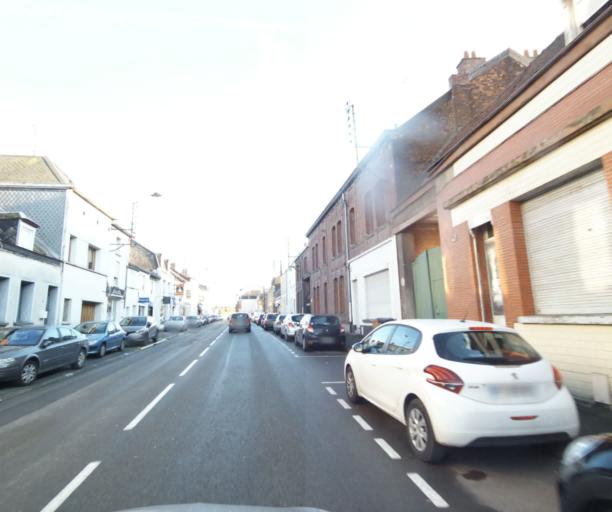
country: FR
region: Nord-Pas-de-Calais
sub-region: Departement du Nord
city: Valenciennes
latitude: 50.3518
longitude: 3.5379
